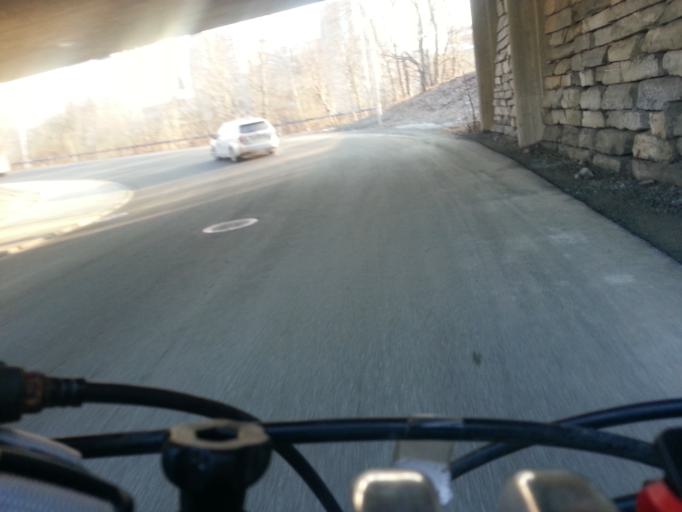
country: NO
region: Sor-Trondelag
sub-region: Trondheim
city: Trondheim
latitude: 63.4184
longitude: 10.3826
